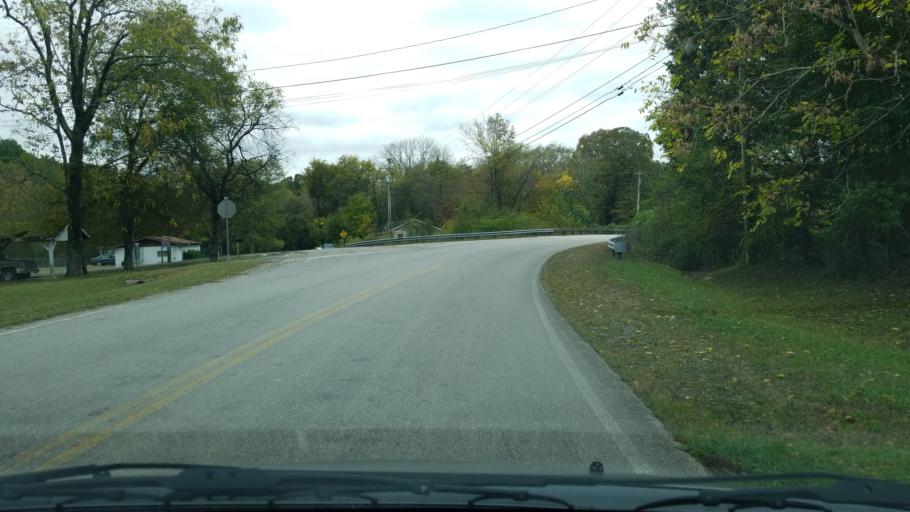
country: US
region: Tennessee
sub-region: Rhea County
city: Dayton
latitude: 35.5090
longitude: -85.0220
